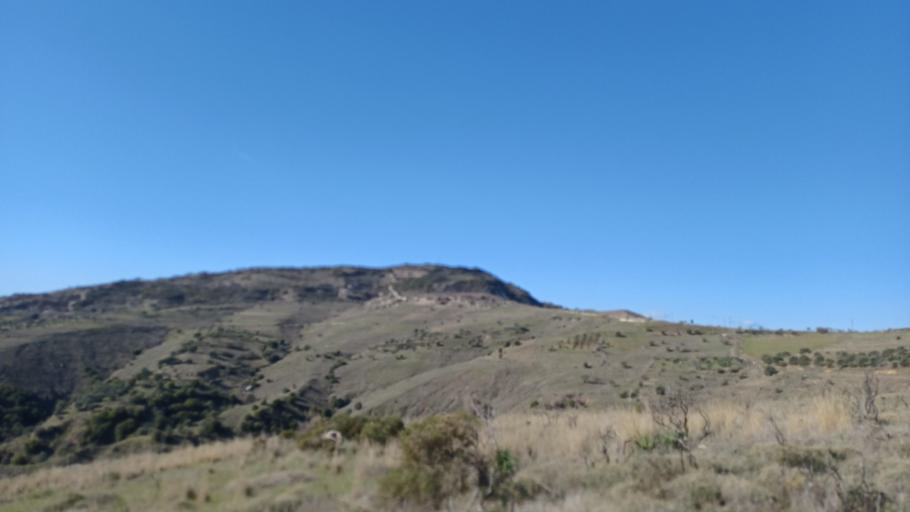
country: CY
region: Limassol
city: Pachna
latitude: 34.8215
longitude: 32.6888
